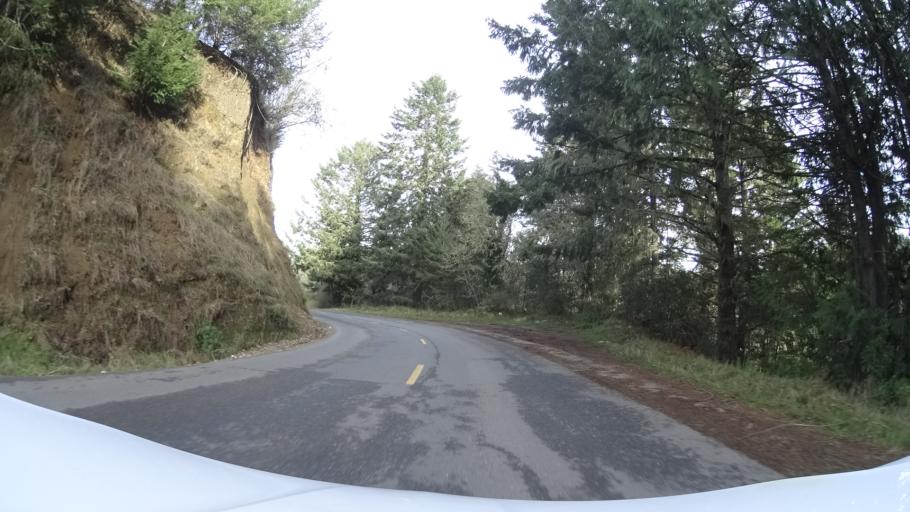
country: US
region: California
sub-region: Humboldt County
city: Ferndale
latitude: 40.5644
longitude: -124.2723
